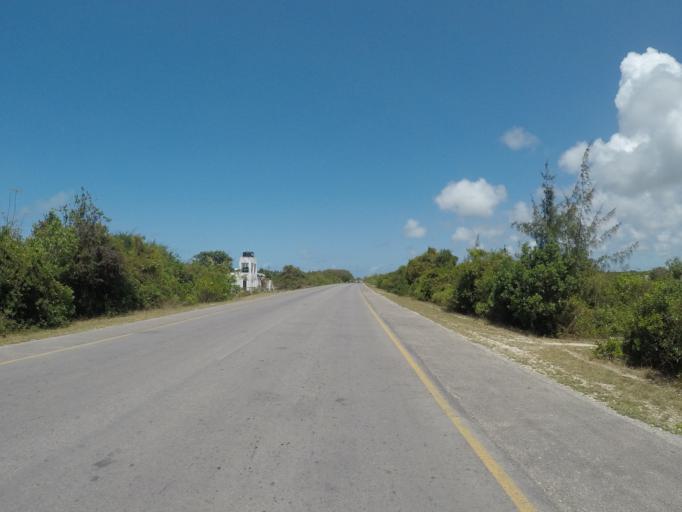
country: TZ
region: Zanzibar Central/South
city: Nganane
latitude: -6.3250
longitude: 39.5461
